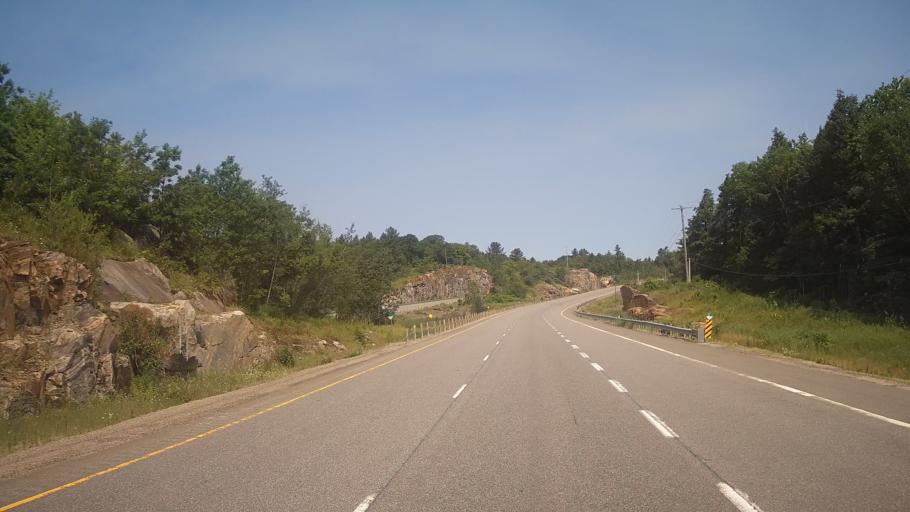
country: CA
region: Ontario
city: Midland
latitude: 44.9929
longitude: -79.7829
